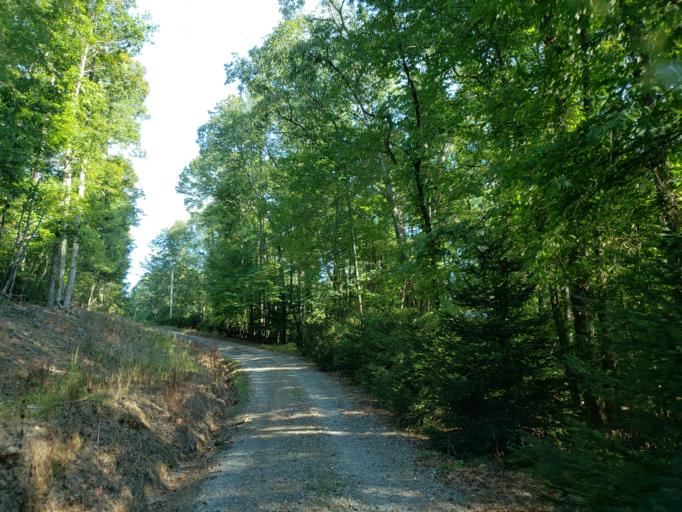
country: US
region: Georgia
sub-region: Fannin County
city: Blue Ridge
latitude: 34.6766
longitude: -84.2673
